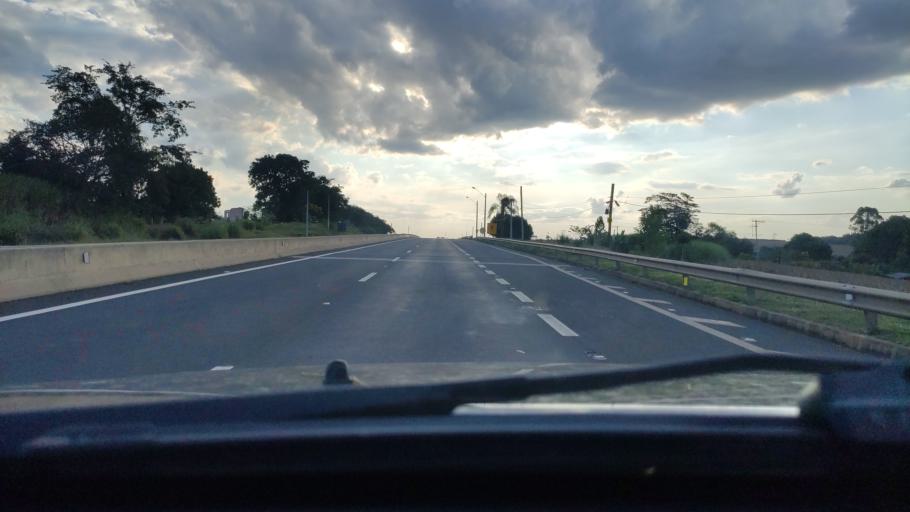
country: BR
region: Sao Paulo
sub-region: Mogi-Mirim
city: Mogi Mirim
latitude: -22.4424
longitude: -47.0428
